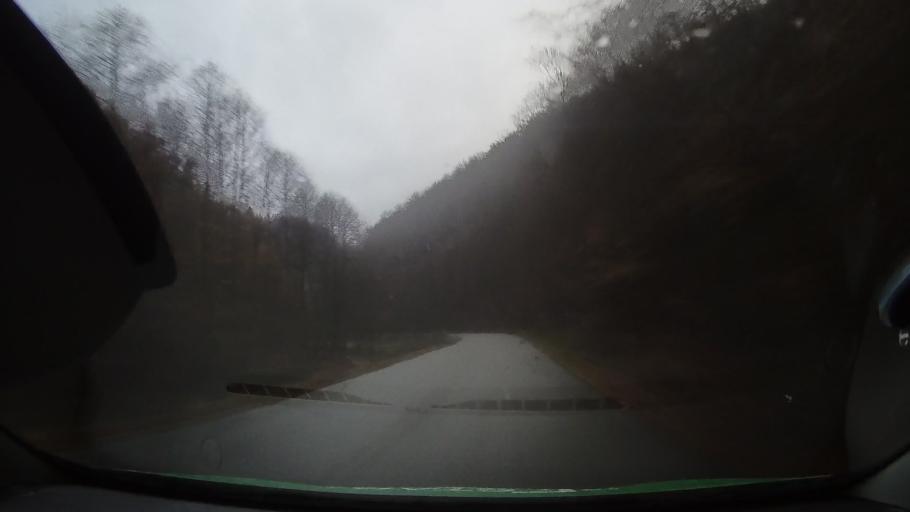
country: RO
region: Hunedoara
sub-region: Comuna Ribita
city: Ribita
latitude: 46.2799
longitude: 22.7377
